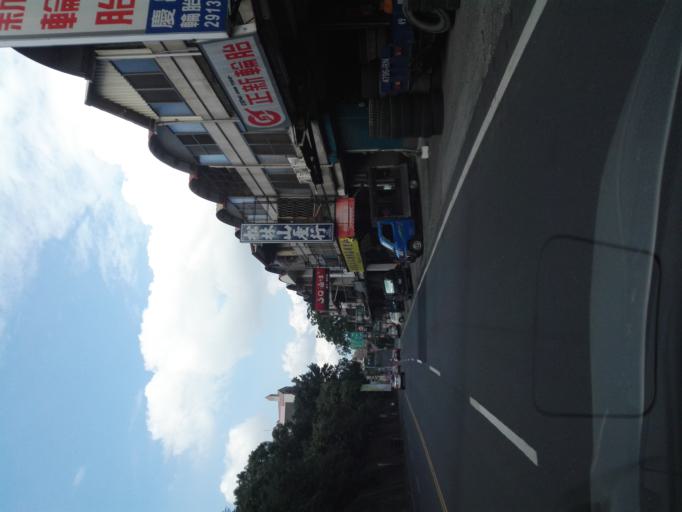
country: TW
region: Taiwan
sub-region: Nantou
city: Puli
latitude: 23.9697
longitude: 120.9471
